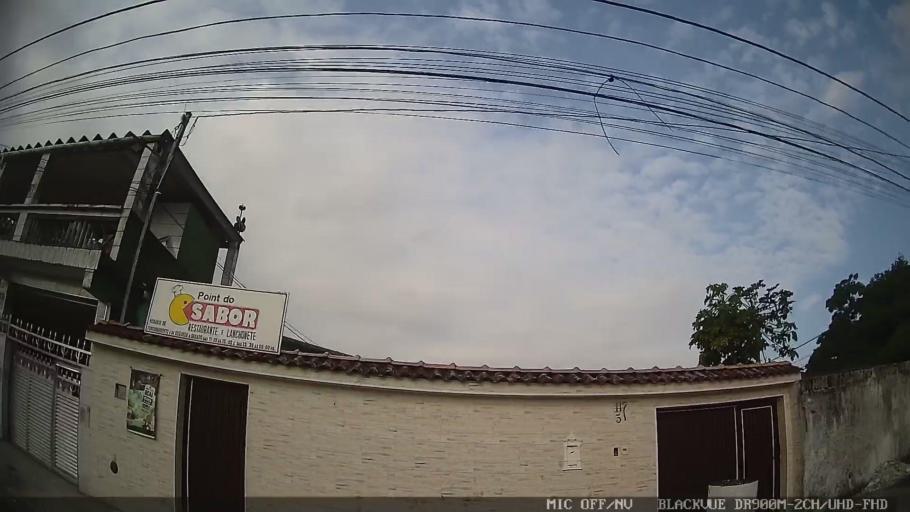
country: BR
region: Sao Paulo
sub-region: Santos
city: Santos
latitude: -23.9524
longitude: -46.2856
